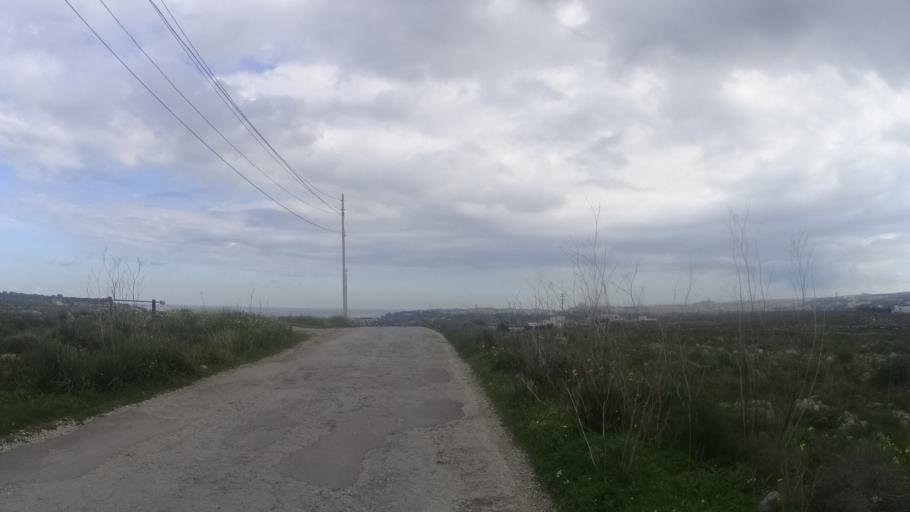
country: MT
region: L-Imgarr
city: Imgarr
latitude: 35.9005
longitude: 14.3757
